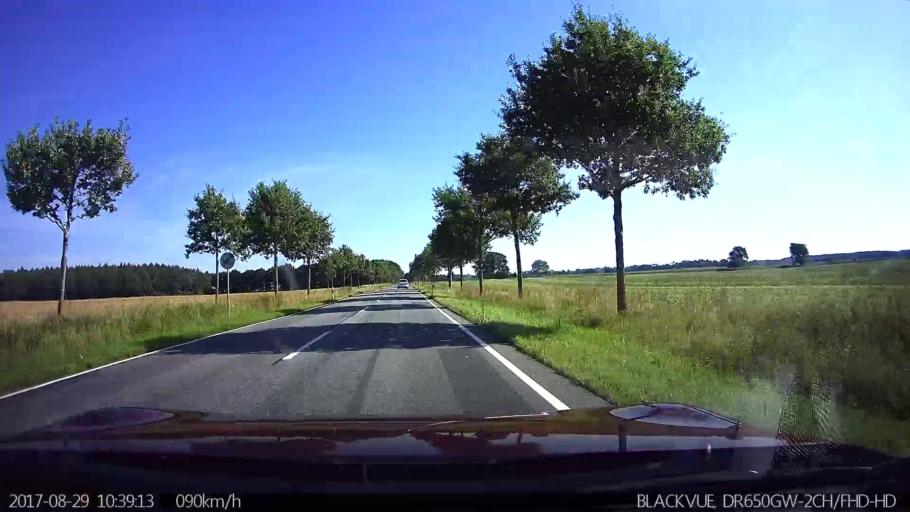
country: DE
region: Mecklenburg-Vorpommern
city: Franzburg
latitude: 54.1731
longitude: 12.8303
